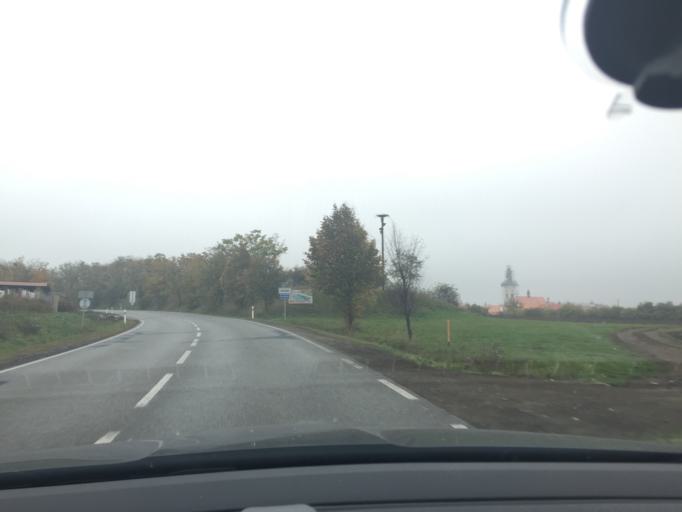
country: CZ
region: South Moravian
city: Rousinov
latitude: 49.1989
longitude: 16.8793
